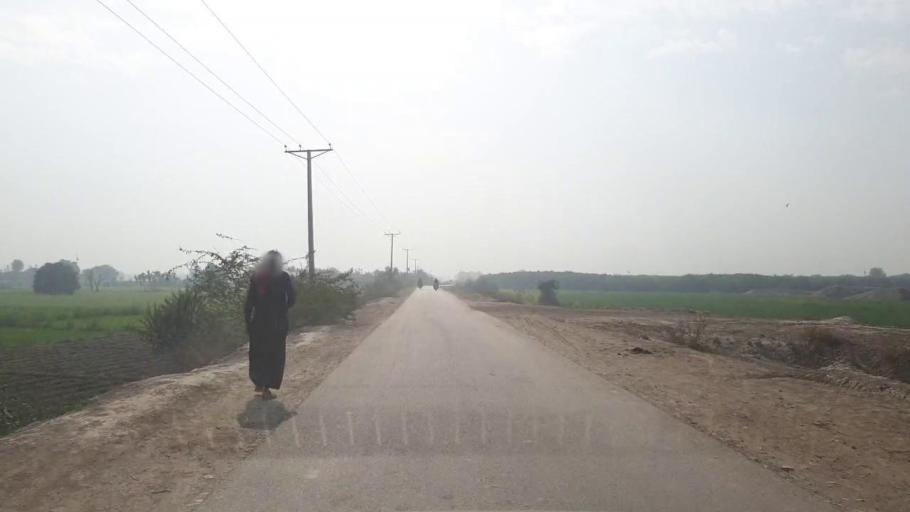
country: PK
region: Sindh
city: Hala
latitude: 25.7672
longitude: 68.4470
